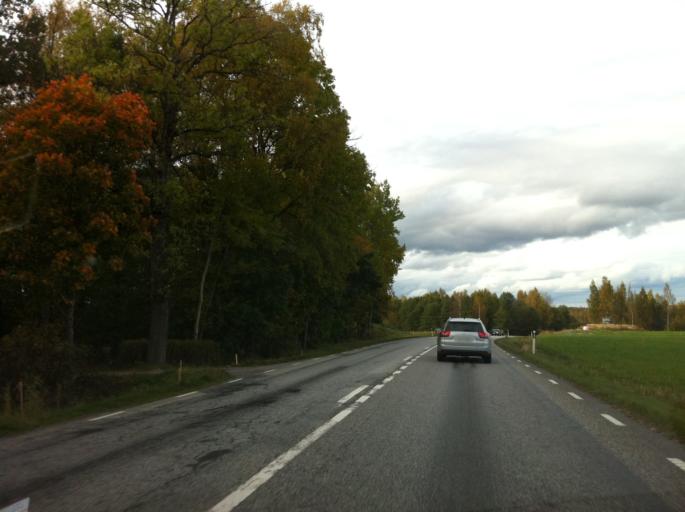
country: SE
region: OErebro
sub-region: Askersunds Kommun
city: Askersund
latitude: 58.8690
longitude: 14.8990
